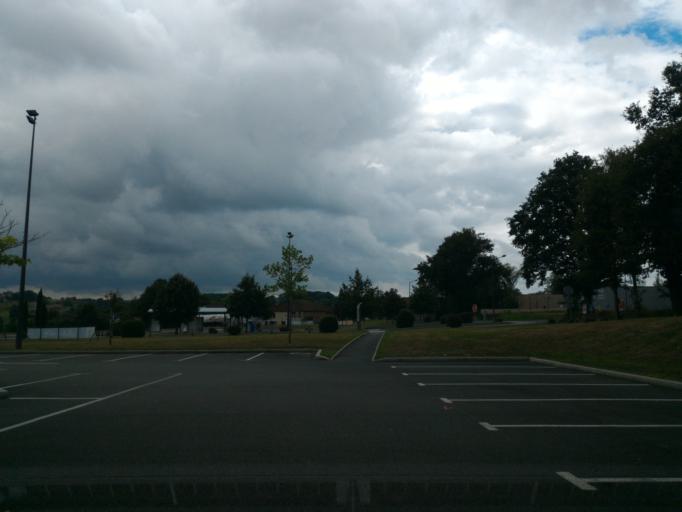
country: FR
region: Poitou-Charentes
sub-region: Departement de la Charente
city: Chabanais
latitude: 45.8816
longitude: 0.7378
